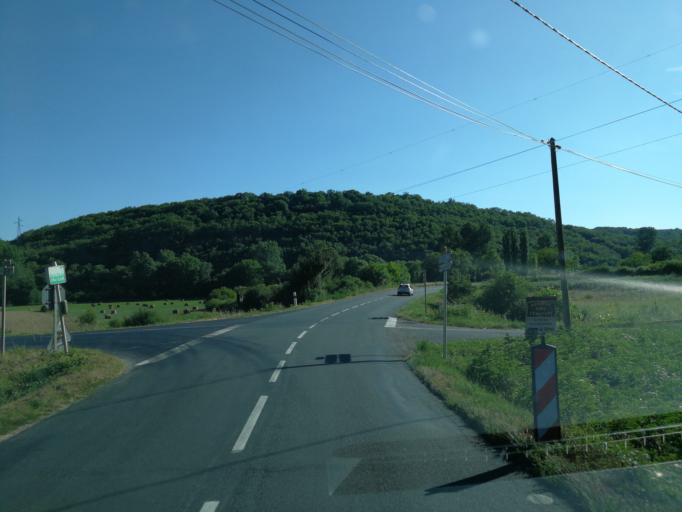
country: FR
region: Midi-Pyrenees
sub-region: Departement du Lot
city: Gourdon
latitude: 44.7080
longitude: 1.3433
